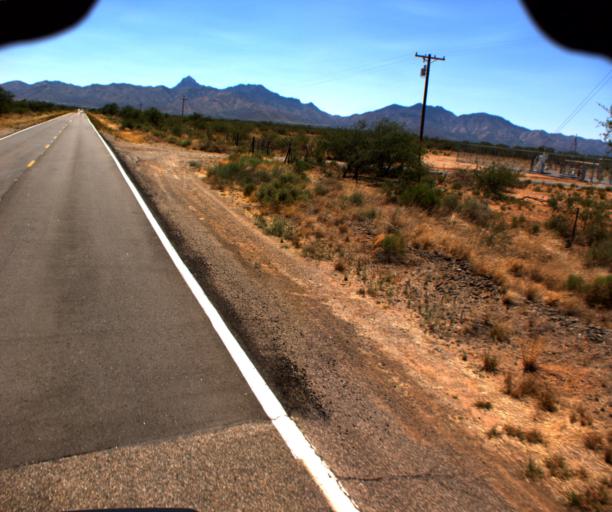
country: US
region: Arizona
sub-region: Pima County
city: Three Points
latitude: 31.8345
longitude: -111.4131
